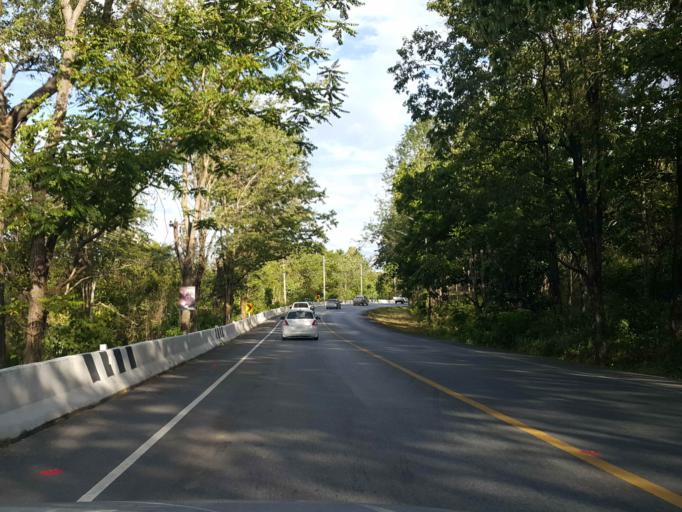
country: TH
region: Tak
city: Tak
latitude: 16.8089
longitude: 98.9932
